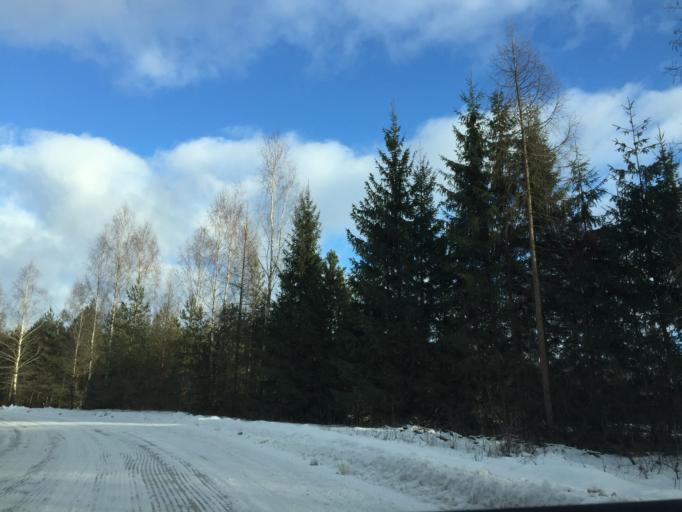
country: LV
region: Ogre
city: Jumprava
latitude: 56.5992
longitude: 24.9979
